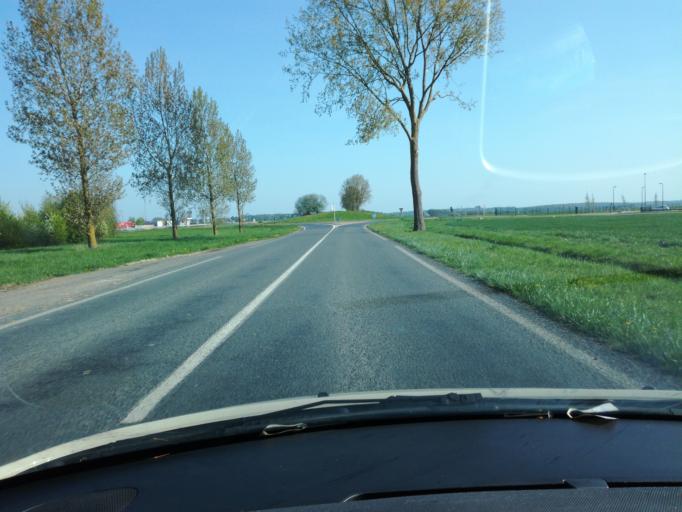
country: FR
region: Picardie
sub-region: Departement de la Somme
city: Poix-de-Picardie
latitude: 49.8089
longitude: 1.9658
